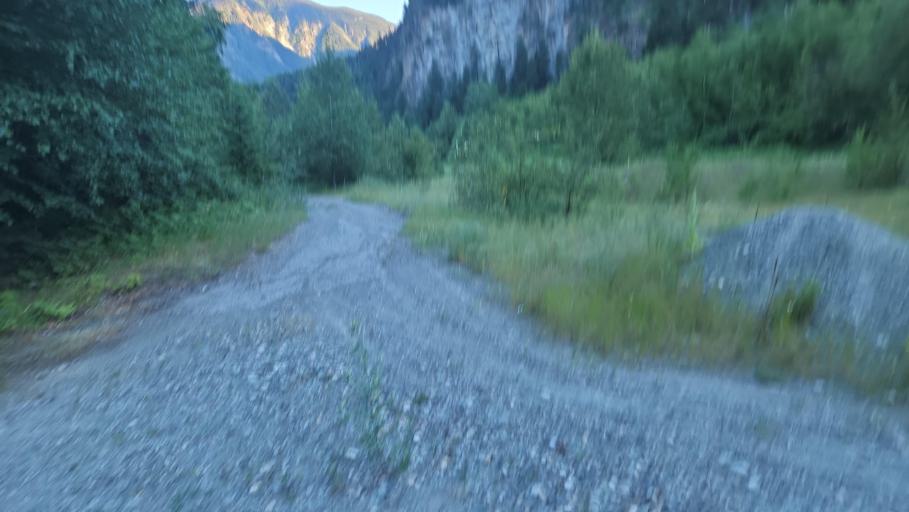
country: CA
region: British Columbia
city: Lillooet
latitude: 50.5838
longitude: -122.0951
